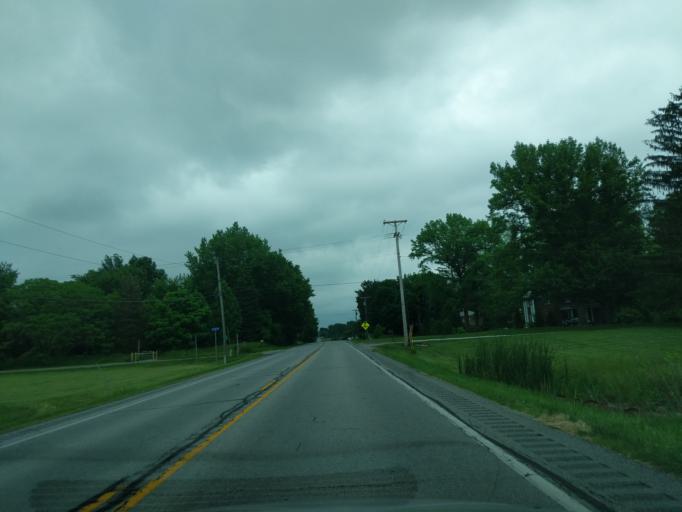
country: US
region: Indiana
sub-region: Madison County
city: Alexandria
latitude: 40.2774
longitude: -85.6957
